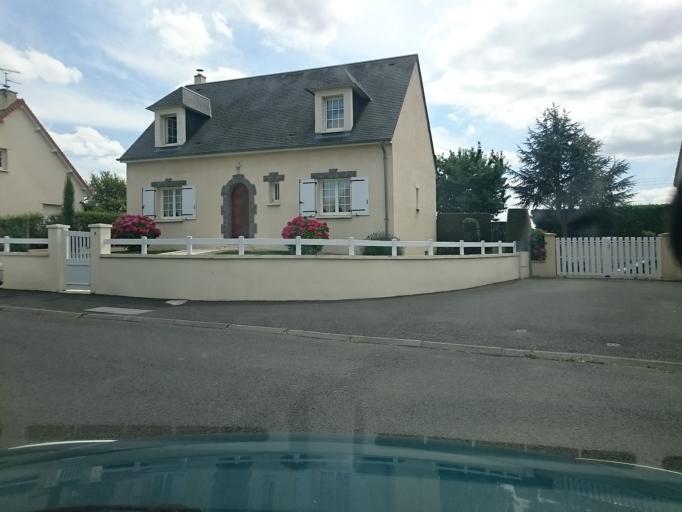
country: FR
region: Lower Normandy
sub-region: Departement du Calvados
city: Ifs
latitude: 49.1354
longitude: -0.3476
